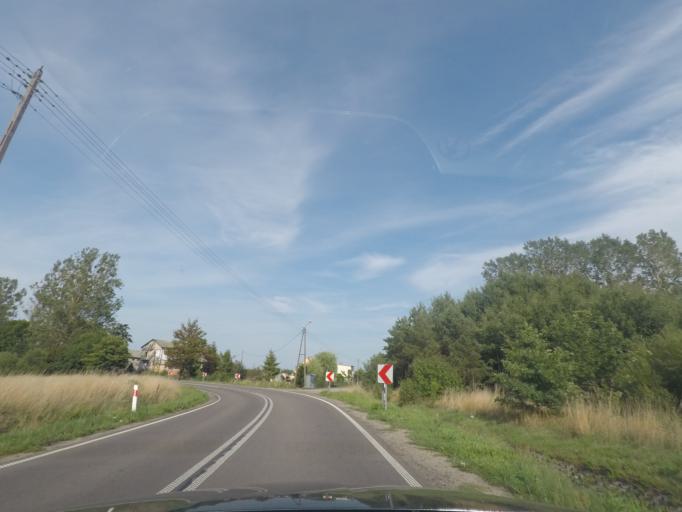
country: PL
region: Pomeranian Voivodeship
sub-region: Powiat leborski
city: Leba
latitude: 54.6452
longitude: 17.5510
